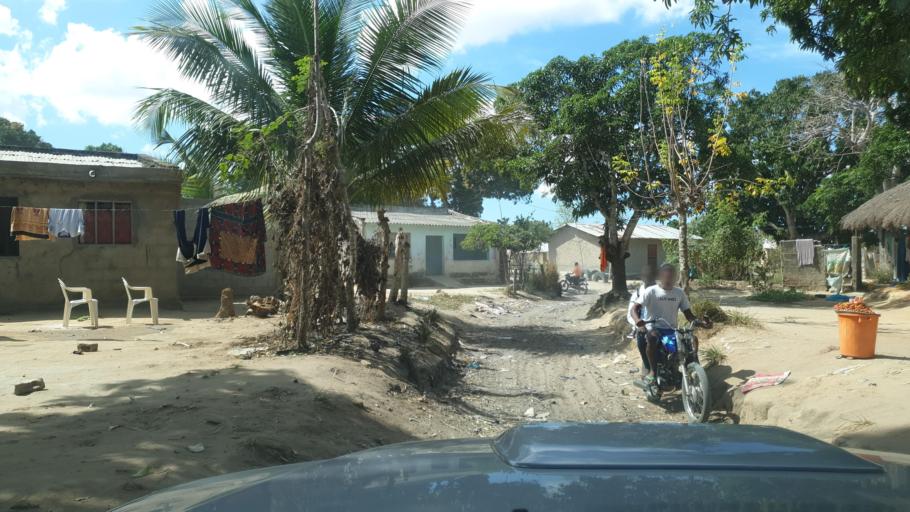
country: MZ
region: Nampula
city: Nacala
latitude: -14.5733
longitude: 40.6968
